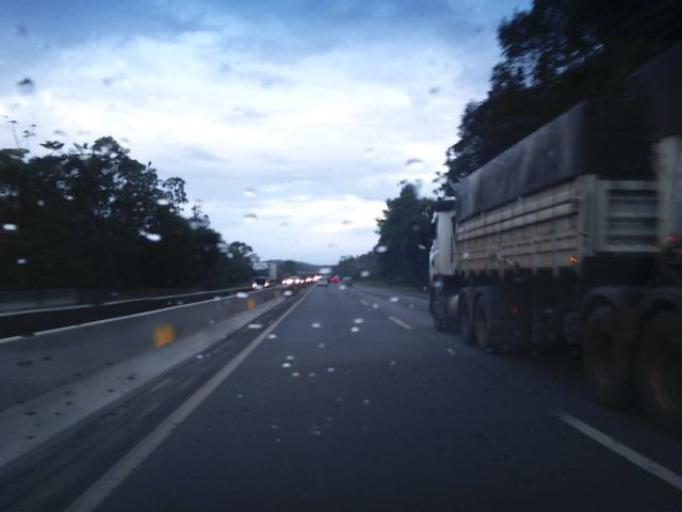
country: BR
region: Santa Catarina
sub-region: Joinville
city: Joinville
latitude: -26.0452
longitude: -48.8596
